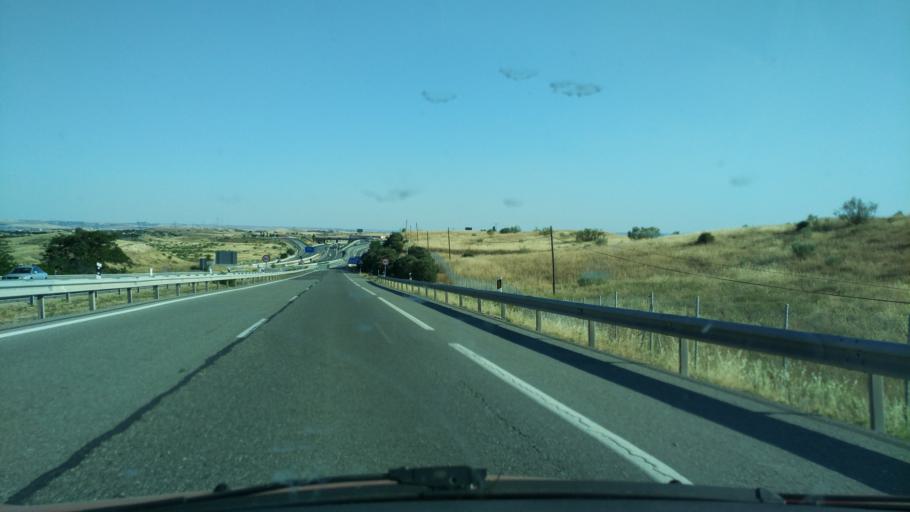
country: ES
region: Madrid
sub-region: Provincia de Madrid
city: El Molar
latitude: 40.7248
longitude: -3.5788
